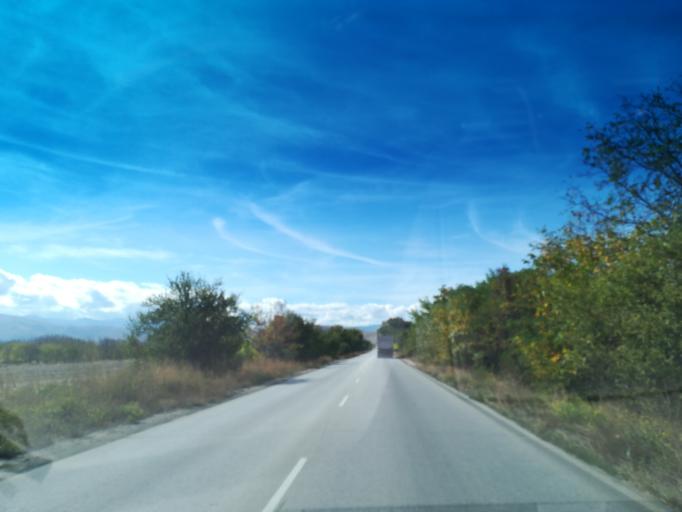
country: BG
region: Plovdiv
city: Stamboliyski
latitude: 42.1124
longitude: 24.5191
